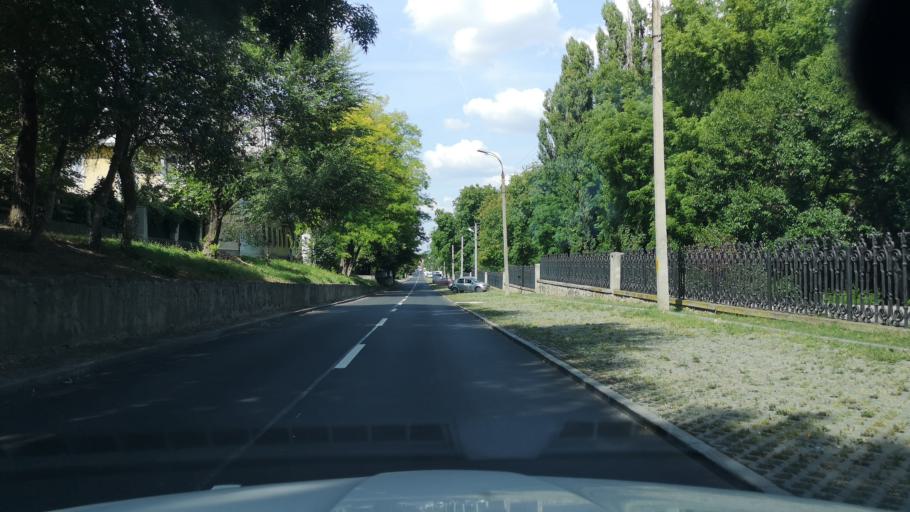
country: MD
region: Chisinau
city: Chisinau
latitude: 47.0235
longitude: 28.8092
